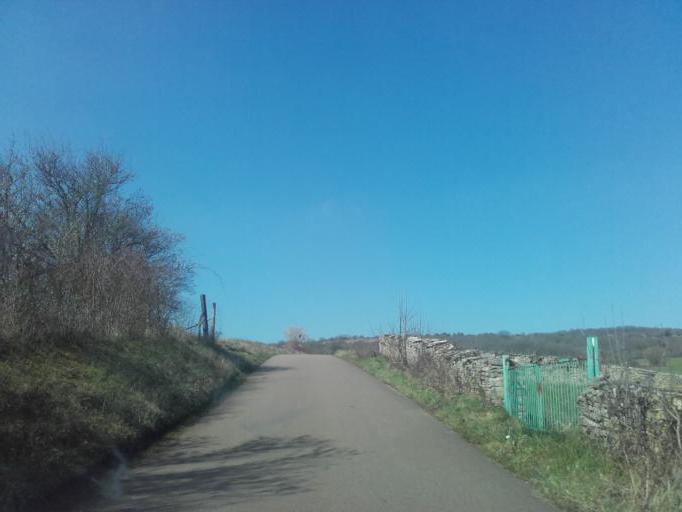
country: FR
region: Bourgogne
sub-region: Departement de la Cote-d'Or
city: Savigny-les-Beaune
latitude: 47.0530
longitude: 4.7666
